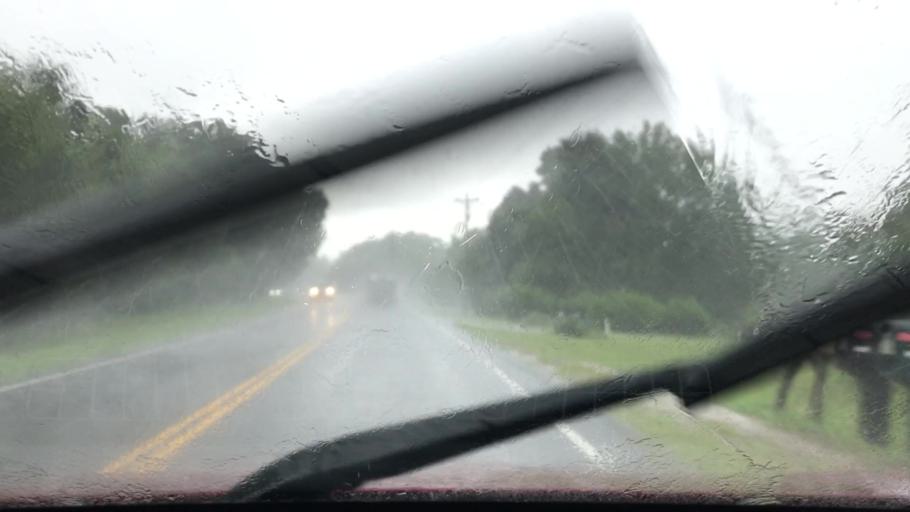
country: US
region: South Carolina
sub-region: Horry County
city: Loris
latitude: 33.9007
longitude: -78.8776
